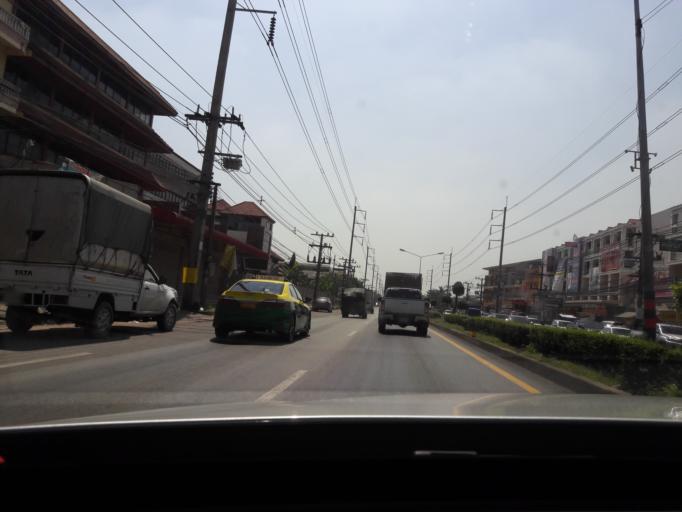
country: TH
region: Samut Sakhon
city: Krathum Baen
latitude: 13.6209
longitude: 100.2915
